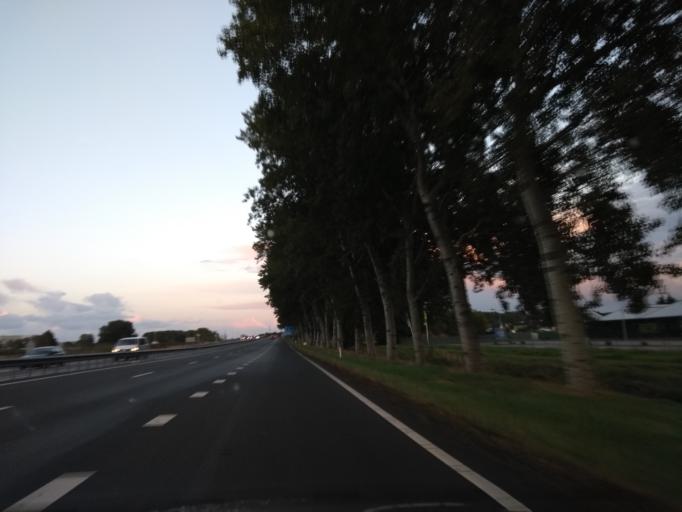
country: NL
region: Friesland
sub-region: Sudwest Fryslan
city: Sneek
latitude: 53.0219
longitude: 5.6647
